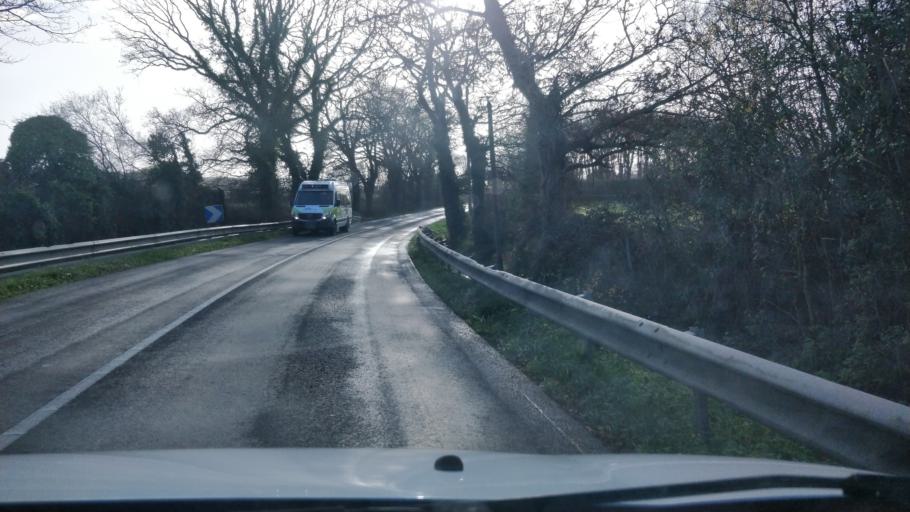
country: FR
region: Pays de la Loire
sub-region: Departement de la Loire-Atlantique
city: Saint-Molf
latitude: 47.3686
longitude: -2.4320
